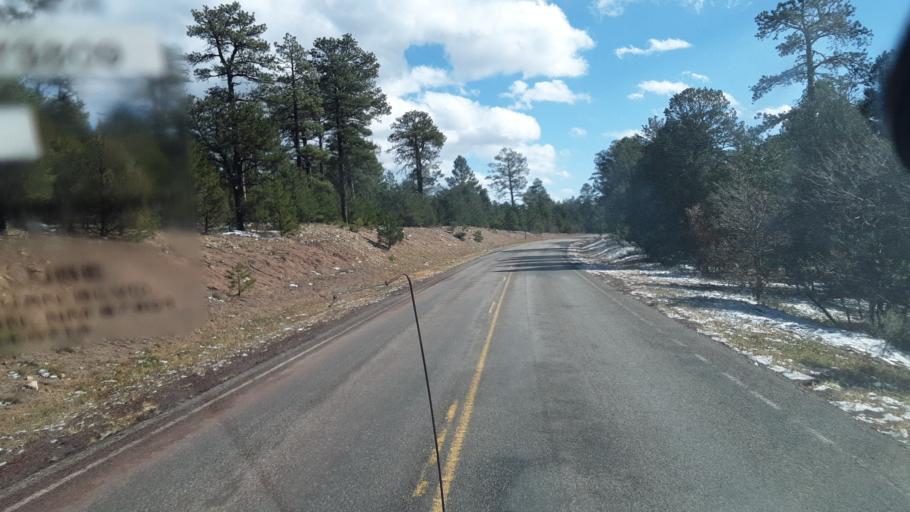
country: US
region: New Mexico
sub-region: Rio Arriba County
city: Santa Teresa
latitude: 36.1984
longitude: -106.7501
